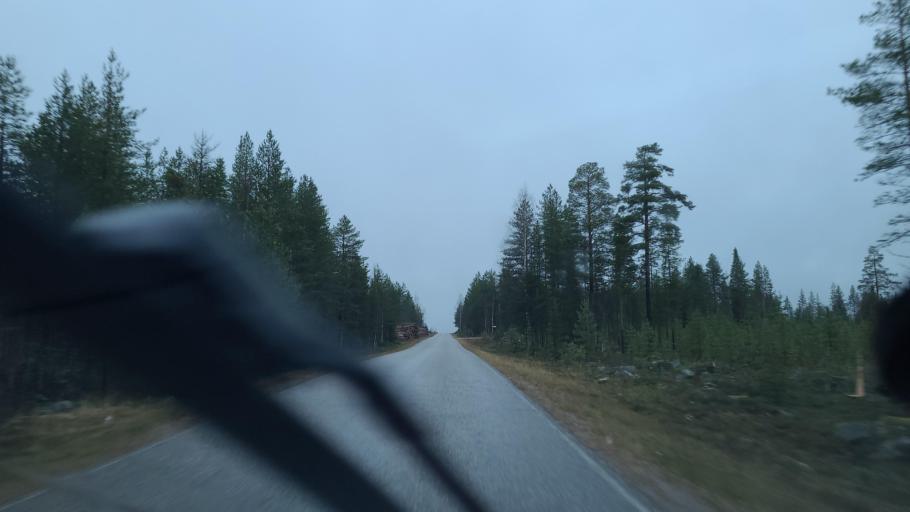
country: FI
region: Lapland
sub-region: Kemi-Tornio
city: Simo
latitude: 65.9074
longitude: 25.2034
